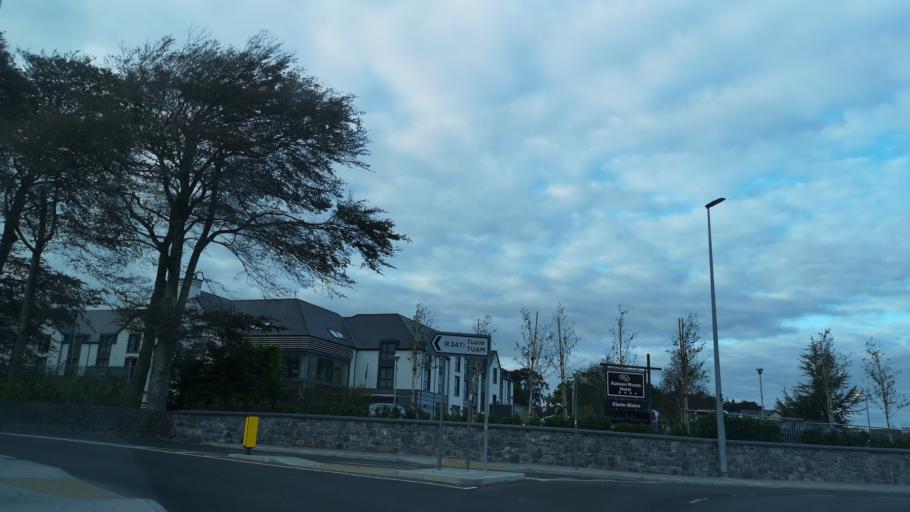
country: IE
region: Connaught
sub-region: County Galway
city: Athenry
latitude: 53.2998
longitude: -8.7613
